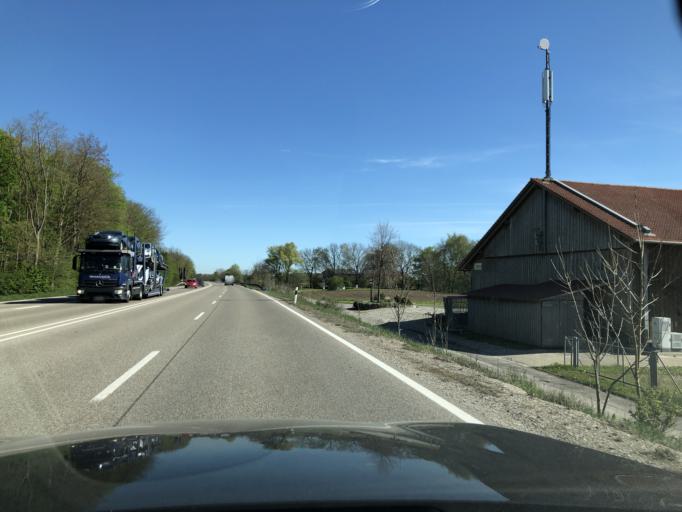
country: DE
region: Bavaria
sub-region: Swabia
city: Jengen
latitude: 48.0051
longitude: 10.7213
